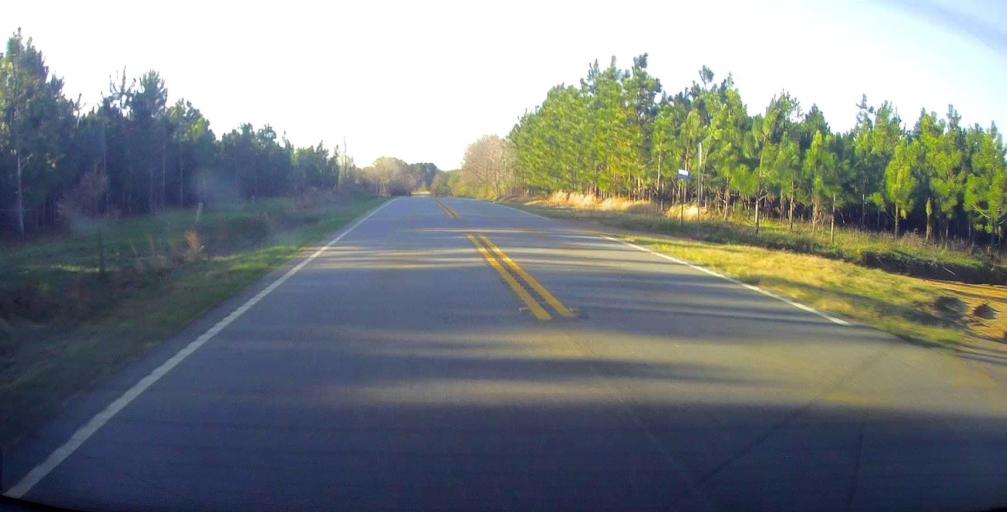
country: US
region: Georgia
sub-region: Wilcox County
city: Abbeville
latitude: 32.1319
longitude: -83.3364
